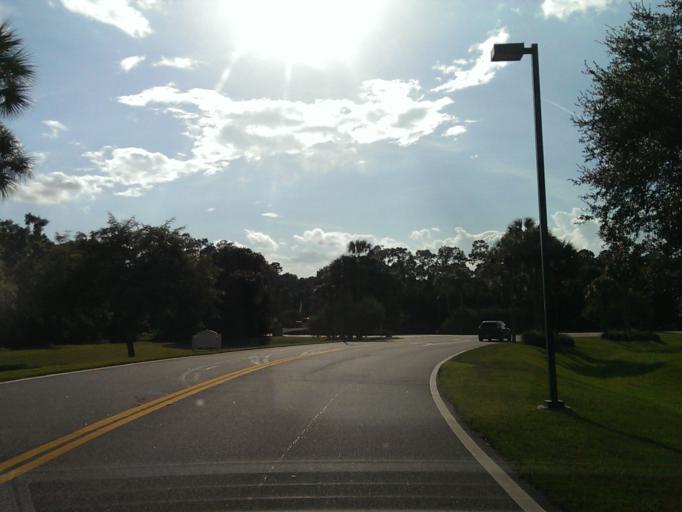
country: US
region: Florida
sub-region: Osceola County
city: Celebration
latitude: 28.3600
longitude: -81.5446
